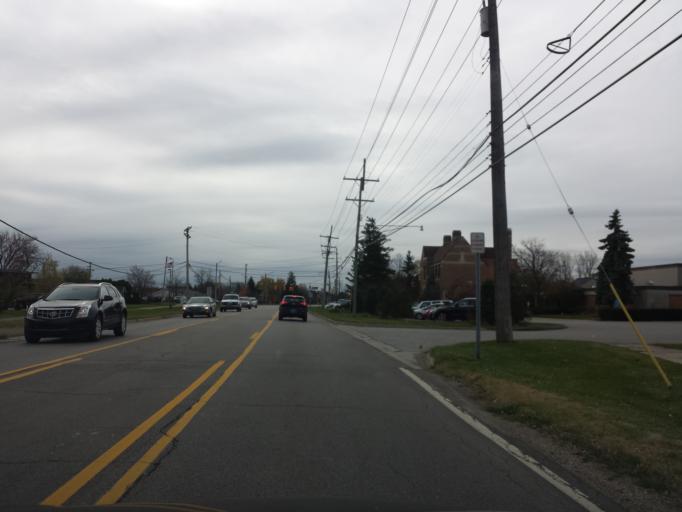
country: US
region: Michigan
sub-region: Oakland County
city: Troy
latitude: 42.6241
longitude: -83.1508
